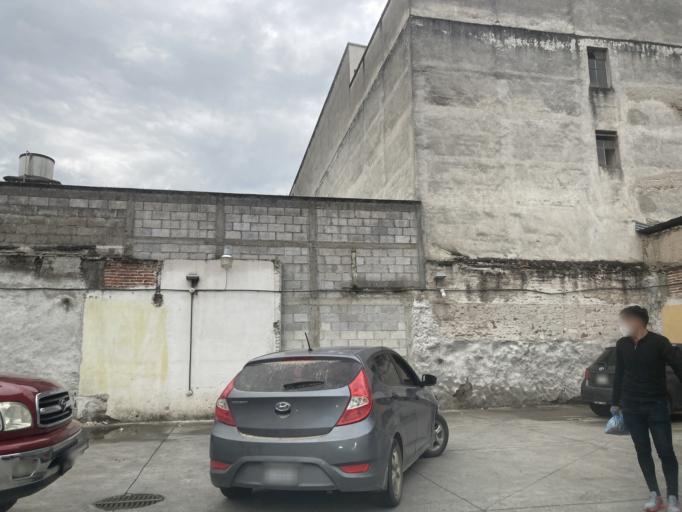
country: GT
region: Huehuetenango
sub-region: Municipio de Huehuetenango
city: Huehuetenango
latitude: 15.3213
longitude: -91.4684
